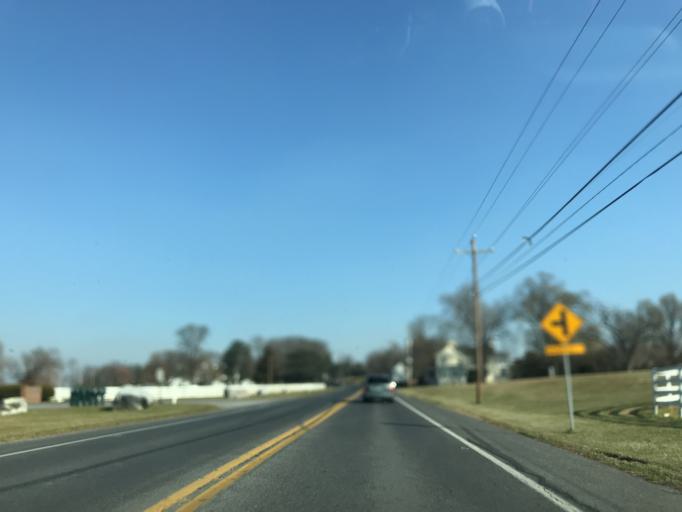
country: US
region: Pennsylvania
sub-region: York County
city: Pennville
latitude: 39.7679
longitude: -77.0242
